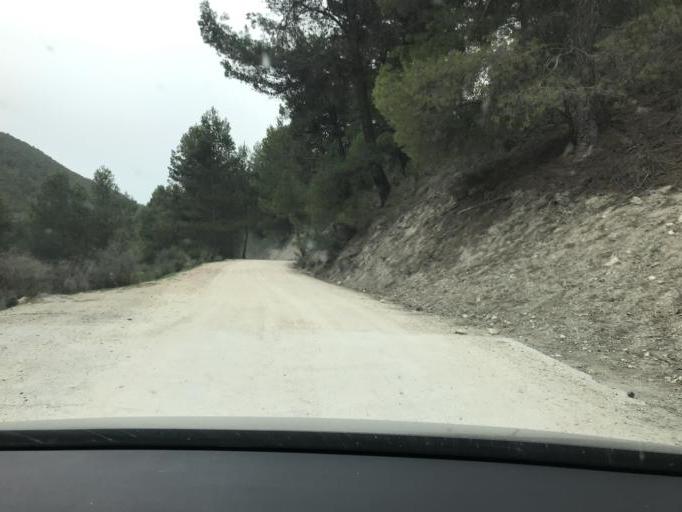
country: ES
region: Andalusia
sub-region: Provincia de Granada
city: Castril
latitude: 37.8617
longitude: -2.7691
